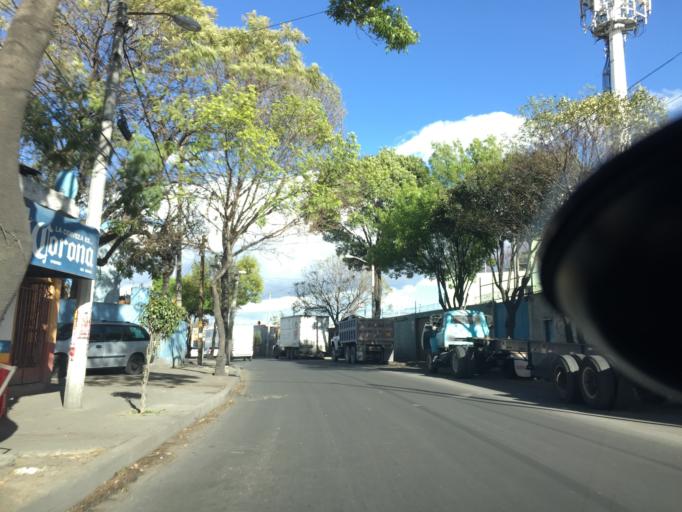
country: MX
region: Mexico City
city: Azcapotzalco
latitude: 19.4877
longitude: -99.1597
